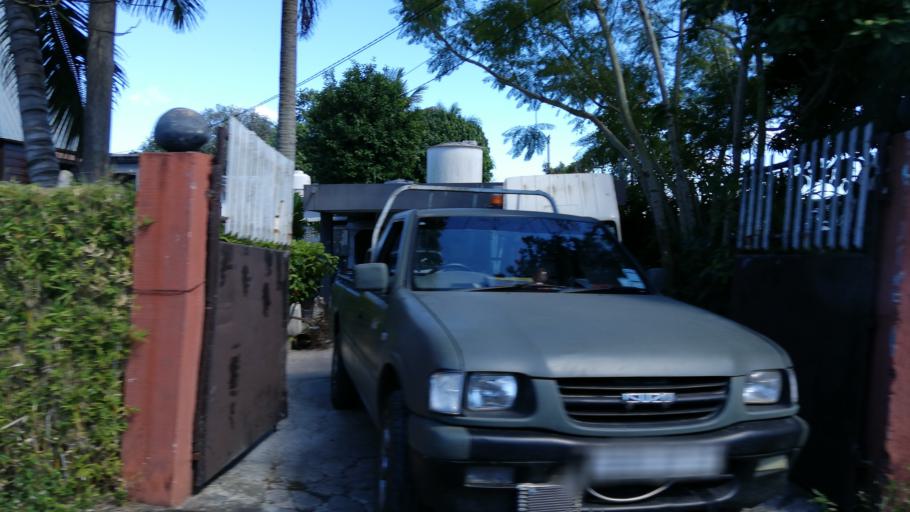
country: MU
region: Plaines Wilhems
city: Ebene
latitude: -20.2299
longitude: 57.4714
